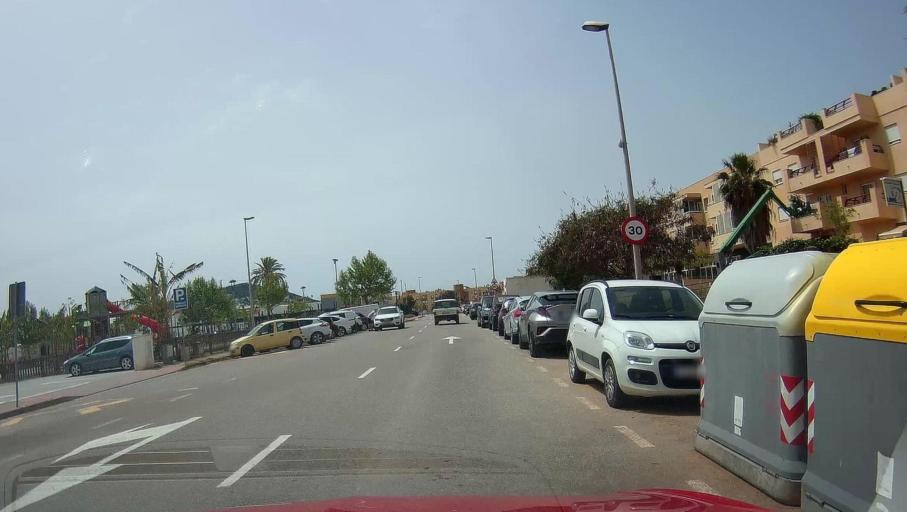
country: ES
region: Balearic Islands
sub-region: Illes Balears
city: Santa Eularia des Riu
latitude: 38.9901
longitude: 1.5453
